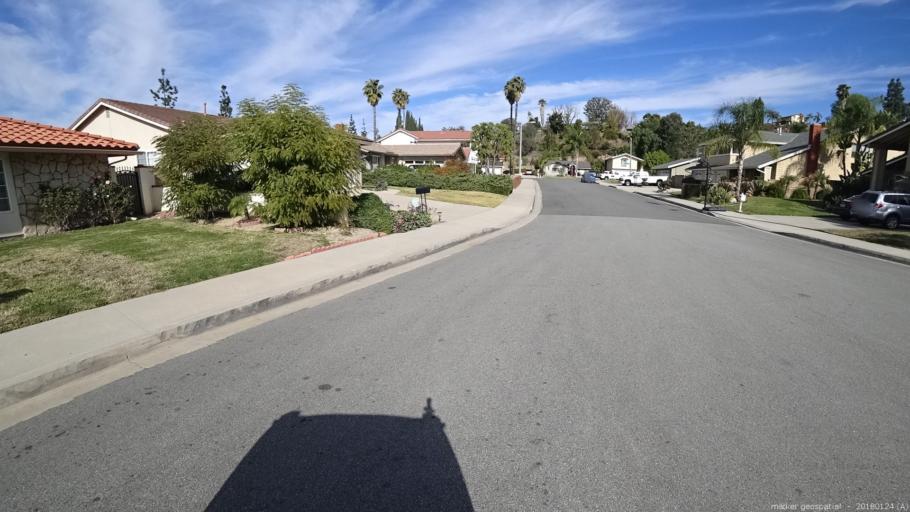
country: US
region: California
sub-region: Los Angeles County
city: Diamond Bar
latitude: 34.0109
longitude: -117.8140
